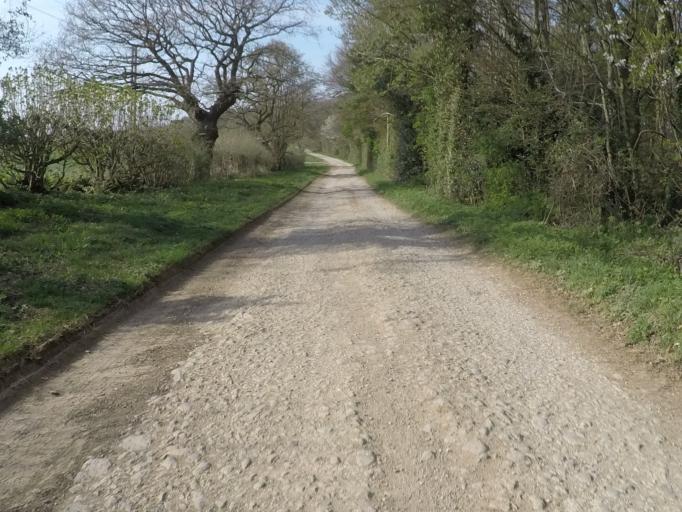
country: GB
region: England
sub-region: Oxfordshire
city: Charlbury
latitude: 51.8854
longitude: -1.4520
